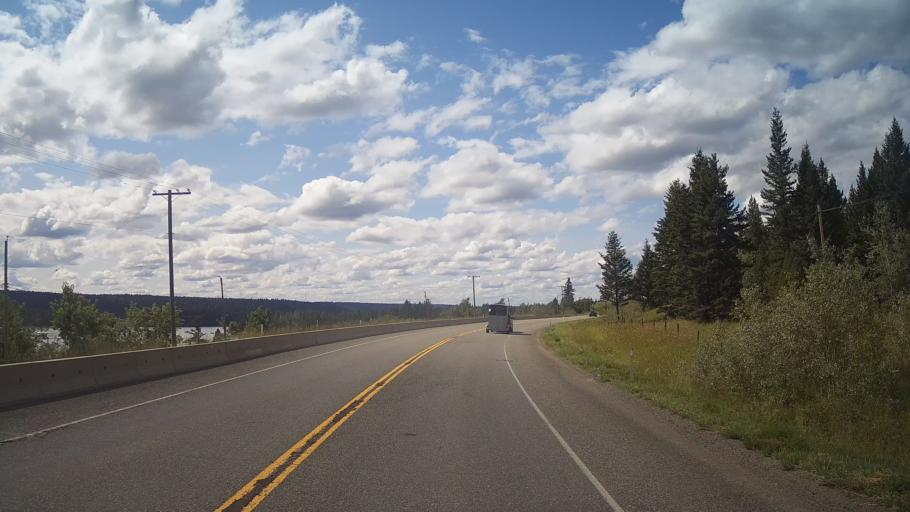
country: CA
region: British Columbia
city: Williams Lake
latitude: 51.8292
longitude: -121.5384
